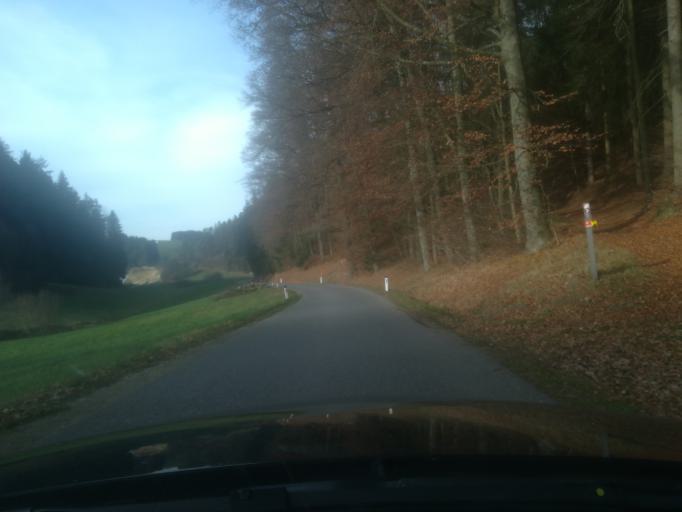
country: AT
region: Upper Austria
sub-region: Politischer Bezirk Perg
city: Perg
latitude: 48.3370
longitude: 14.6464
